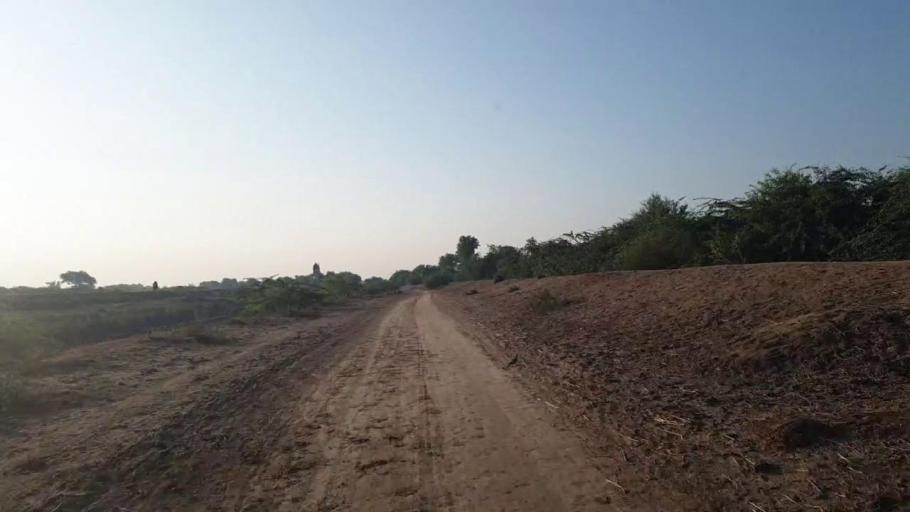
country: PK
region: Sindh
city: Badin
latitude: 24.6396
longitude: 68.7916
